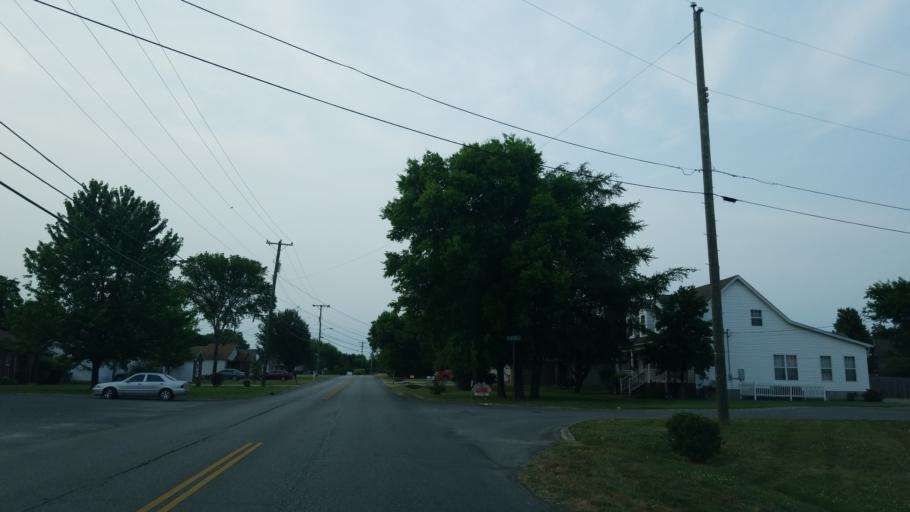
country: US
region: Tennessee
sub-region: Rutherford County
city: La Vergne
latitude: 36.0310
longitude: -86.5886
